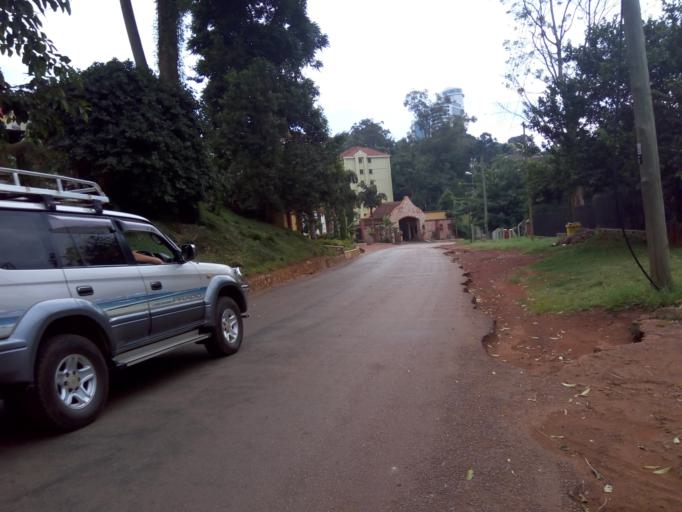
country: UG
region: Central Region
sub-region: Kampala District
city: Kampala
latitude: 0.3224
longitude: 32.5830
